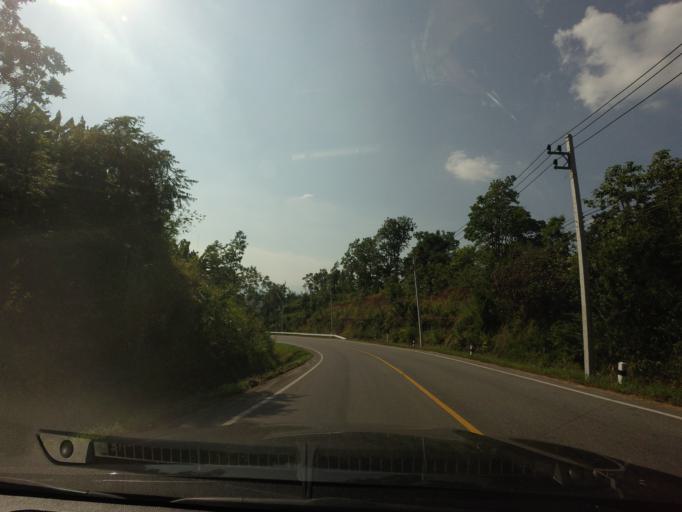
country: TH
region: Nan
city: Santi Suk
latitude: 18.9073
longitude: 100.8568
